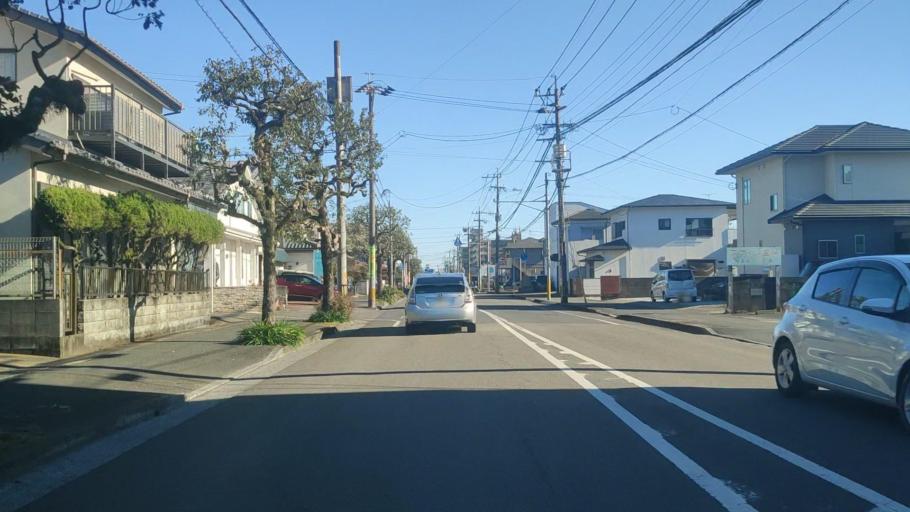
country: JP
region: Miyazaki
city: Miyazaki-shi
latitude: 31.8972
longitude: 131.4277
